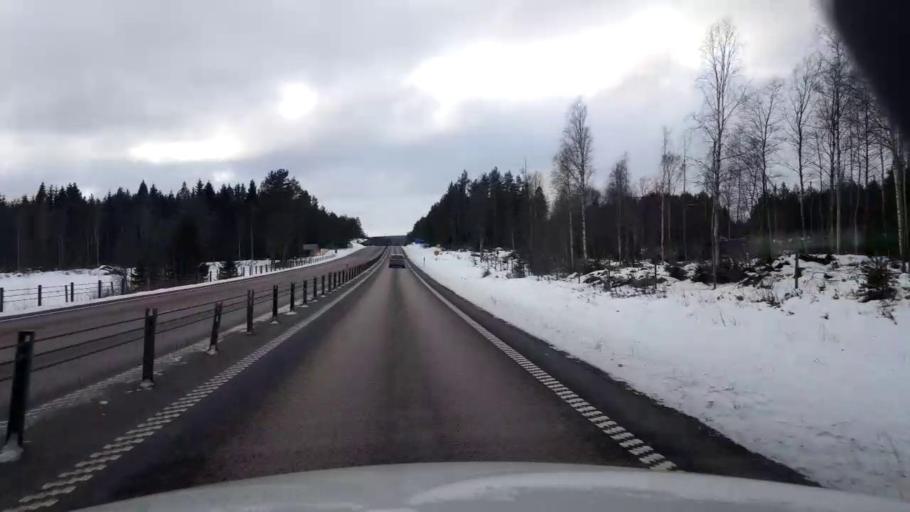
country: SE
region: Gaevleborg
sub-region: Hudiksvalls Kommun
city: Hudiksvall
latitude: 61.8083
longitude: 17.1836
